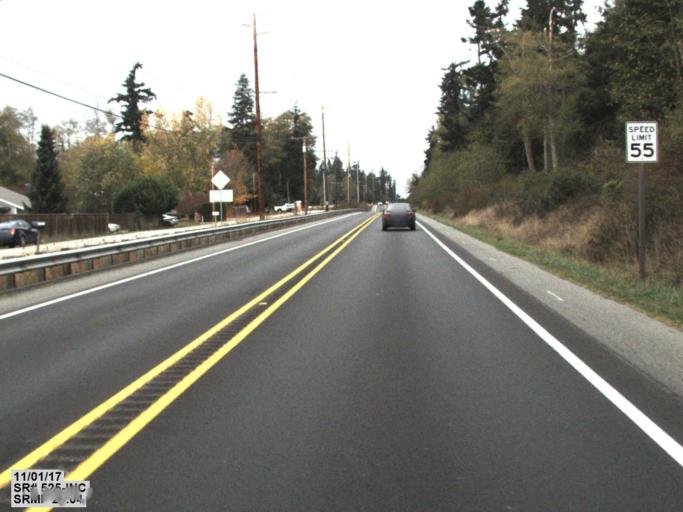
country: US
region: Washington
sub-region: Island County
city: Camano
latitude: 48.1384
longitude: -122.5919
